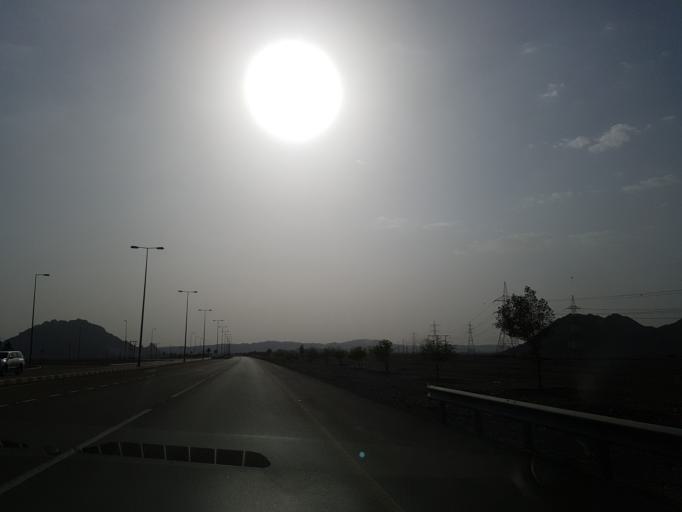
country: OM
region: Al Buraimi
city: Al Buraymi
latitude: 24.2465
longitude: 56.0053
